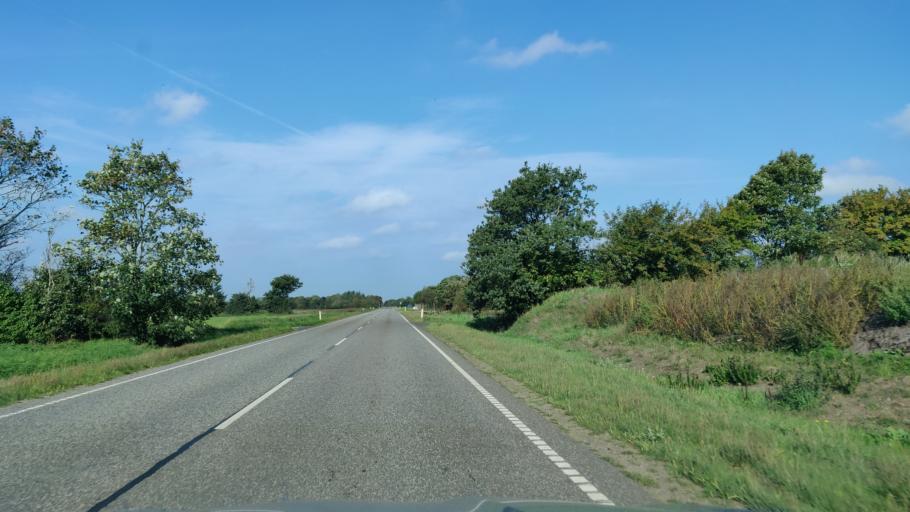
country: DK
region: Central Jutland
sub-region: Herning Kommune
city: Sunds
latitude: 56.2518
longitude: 9.0546
